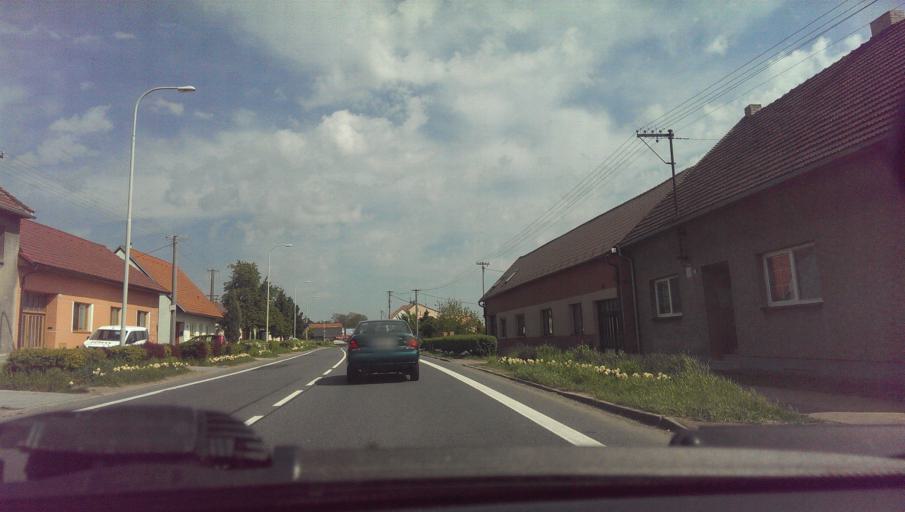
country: CZ
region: Zlin
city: Spytihnev
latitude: 49.1434
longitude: 17.4992
